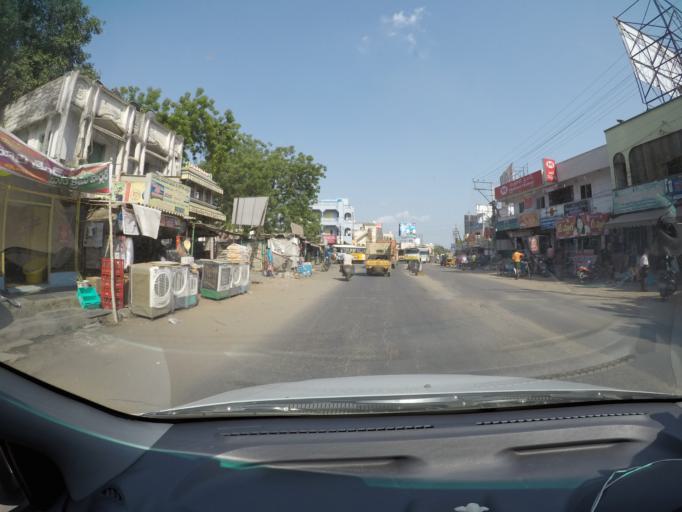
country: IN
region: Andhra Pradesh
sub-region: Krishna
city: Kankipadu
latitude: 16.4347
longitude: 80.7676
